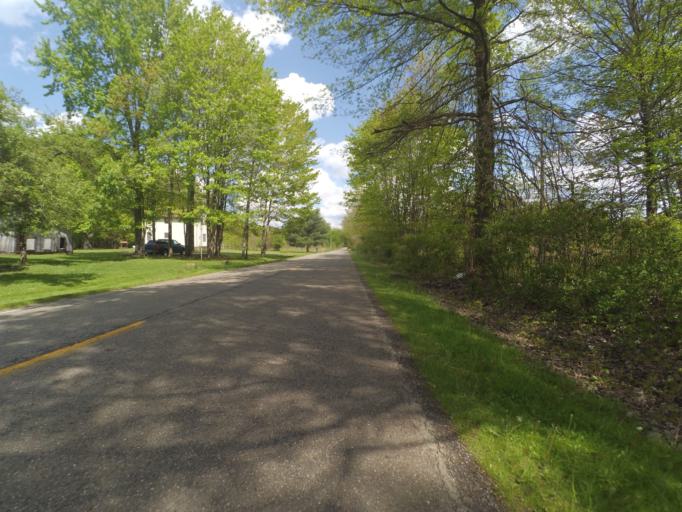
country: US
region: Ohio
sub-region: Trumbull County
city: Lordstown
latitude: 41.1272
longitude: -80.8922
